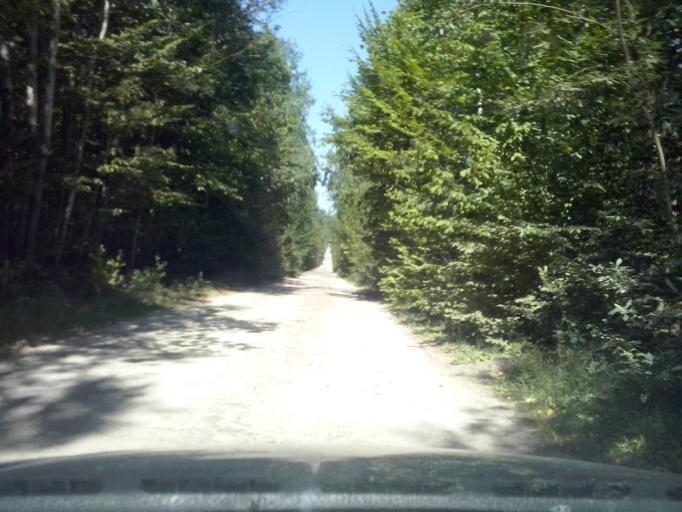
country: PL
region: Swietokrzyskie
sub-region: Powiat kielecki
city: Bieliny
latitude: 50.7922
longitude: 20.9400
